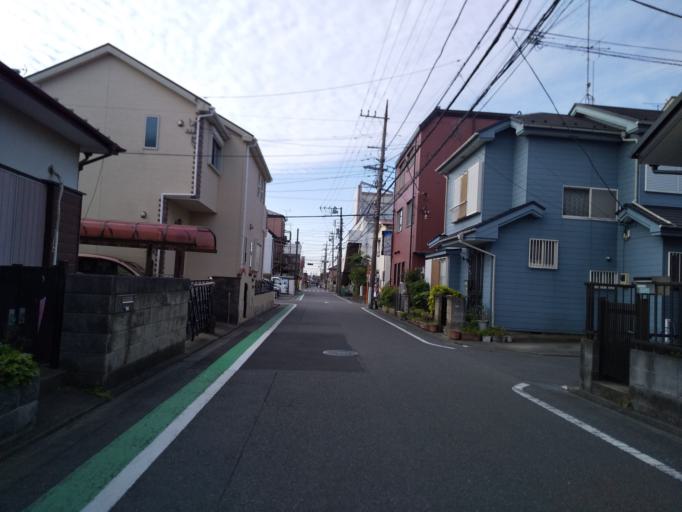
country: JP
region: Kanagawa
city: Zama
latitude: 35.5607
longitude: 139.3802
